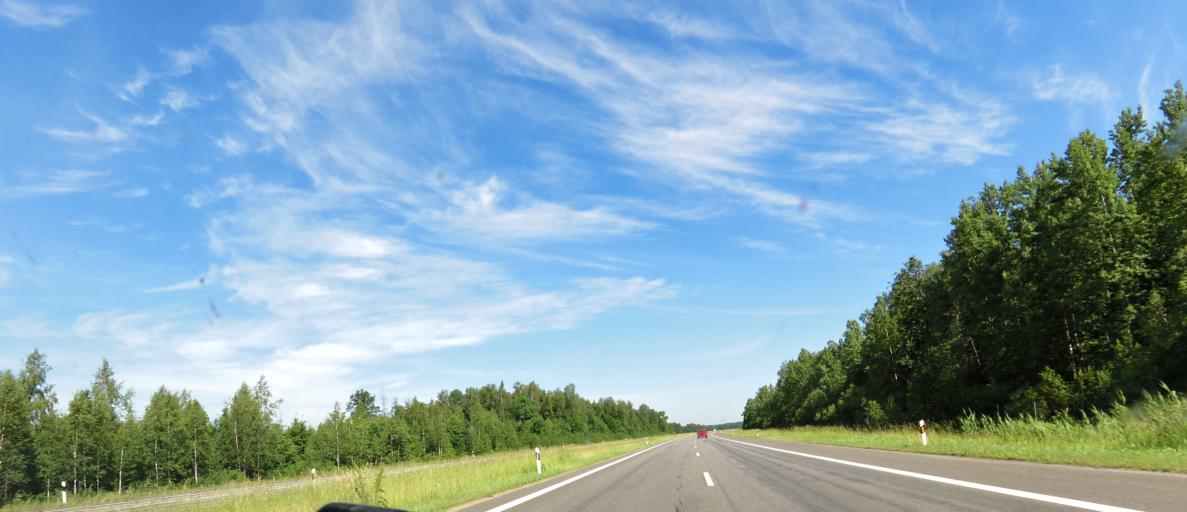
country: LT
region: Vilnius County
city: Ukmerge
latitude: 55.4343
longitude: 24.6752
